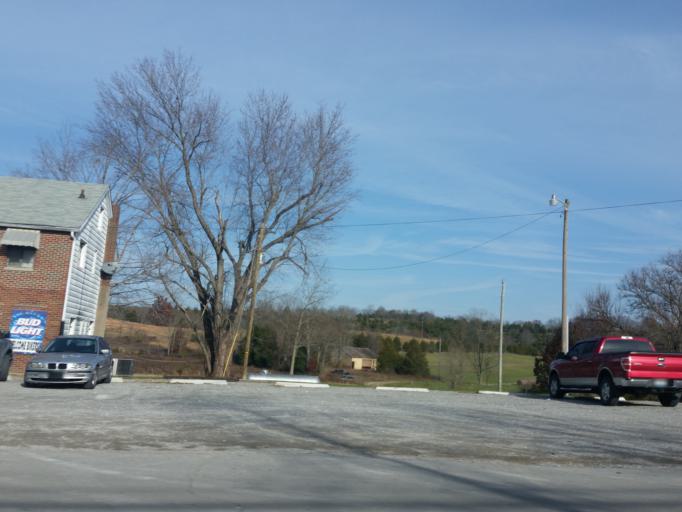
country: US
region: Kentucky
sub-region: Campbell County
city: Claryville
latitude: 38.8358
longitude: -84.3678
